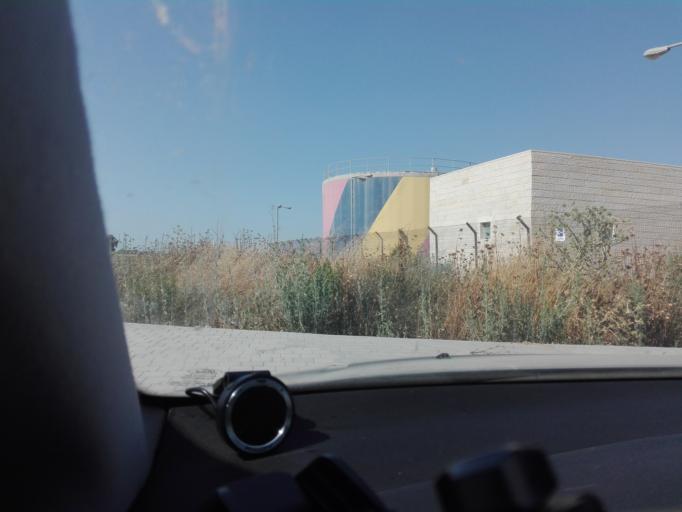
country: IL
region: Central District
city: Bene 'Ayish
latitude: 31.7261
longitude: 34.7601
